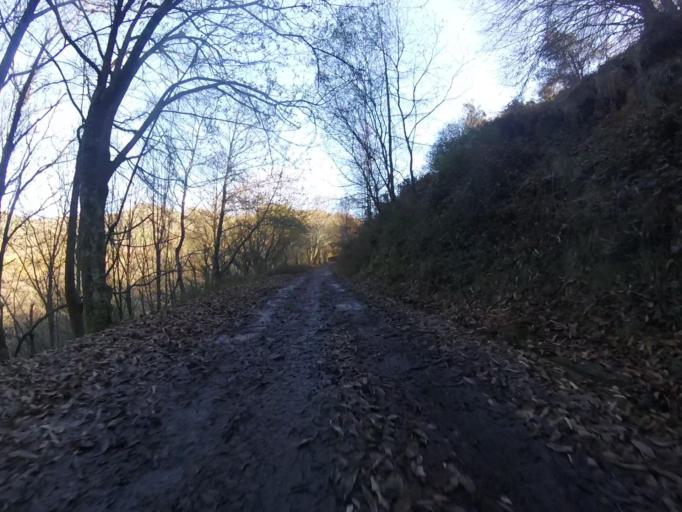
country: ES
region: Navarre
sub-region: Provincia de Navarra
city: Bera
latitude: 43.2999
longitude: -1.6672
